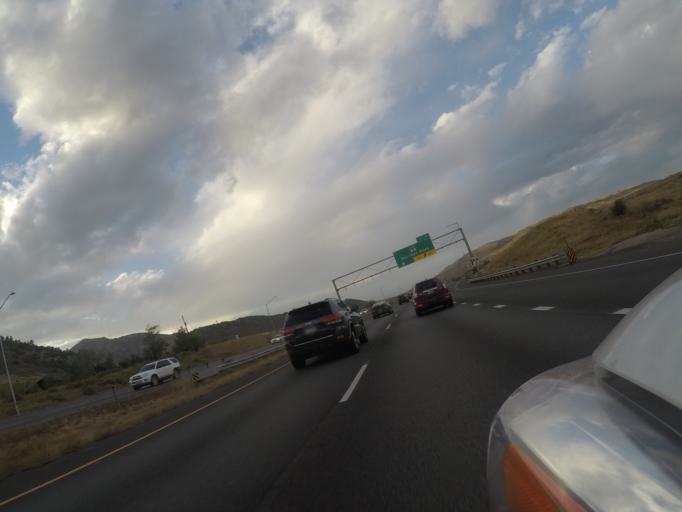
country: US
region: Colorado
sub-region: Jefferson County
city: Indian Hills
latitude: 39.6482
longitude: -105.1806
